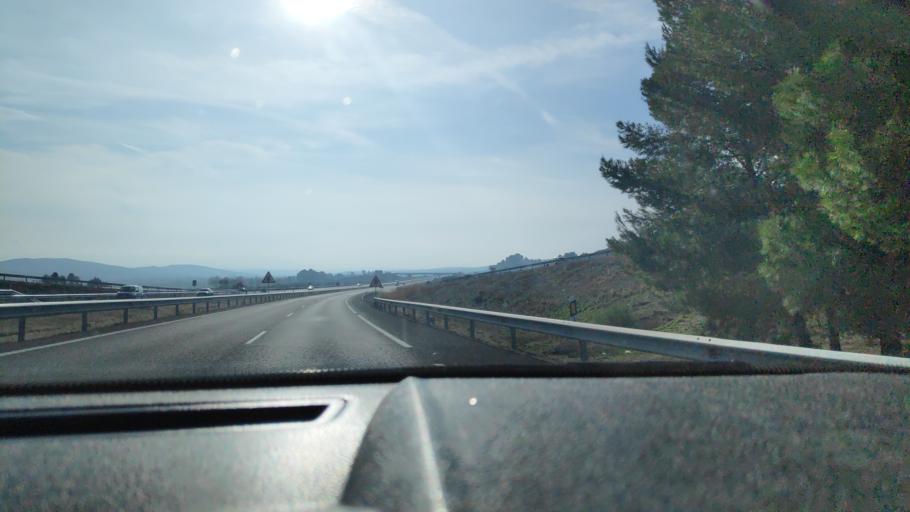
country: ES
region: Andalusia
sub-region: Provincia de Jaen
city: Mengibar
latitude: 37.9085
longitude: -3.7846
